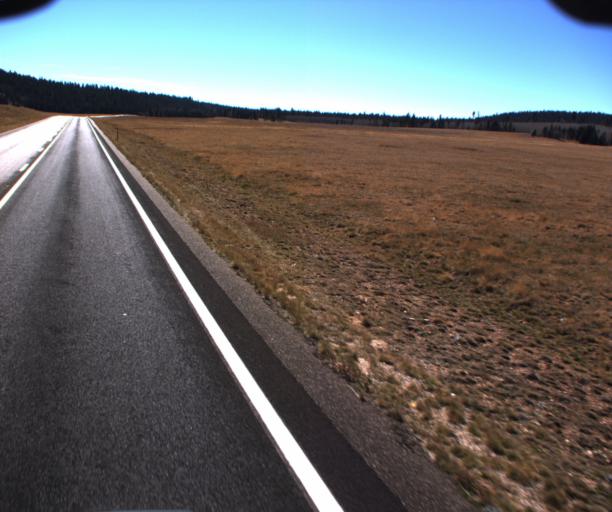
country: US
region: Arizona
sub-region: Coconino County
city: Grand Canyon
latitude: 36.4839
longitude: -112.1283
